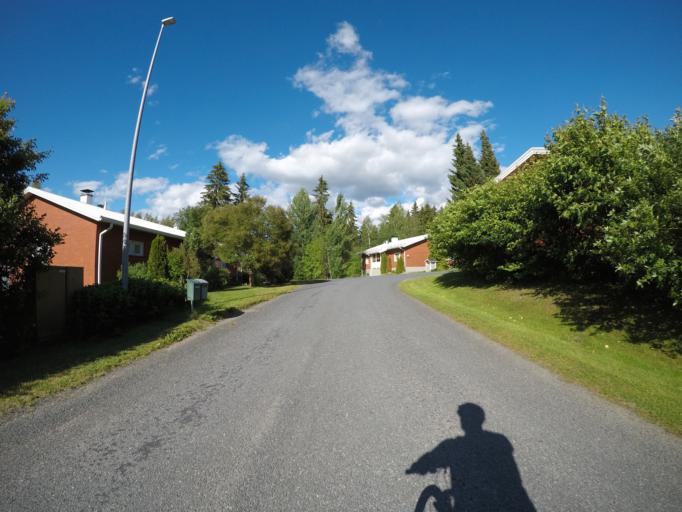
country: FI
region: Haeme
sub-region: Haemeenlinna
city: Haemeenlinna
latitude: 61.0190
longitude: 24.5133
